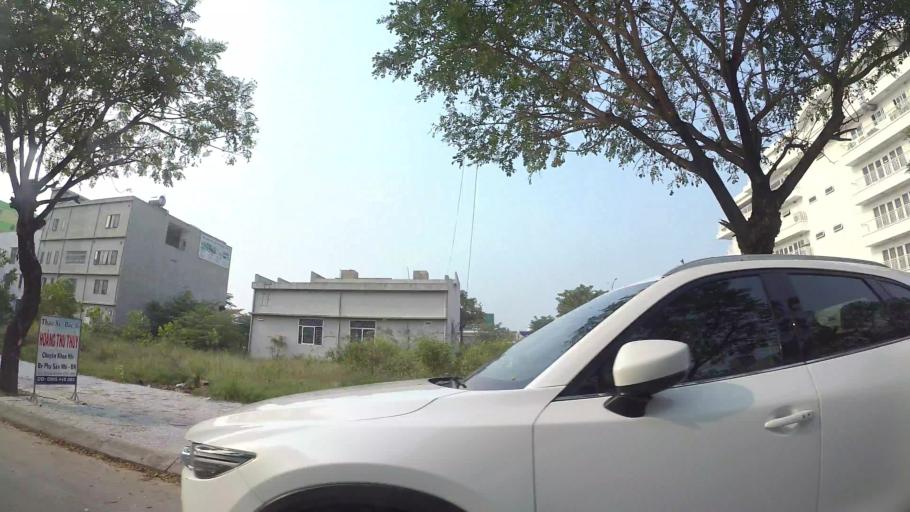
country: VN
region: Da Nang
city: Cam Le
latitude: 16.0047
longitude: 108.2241
